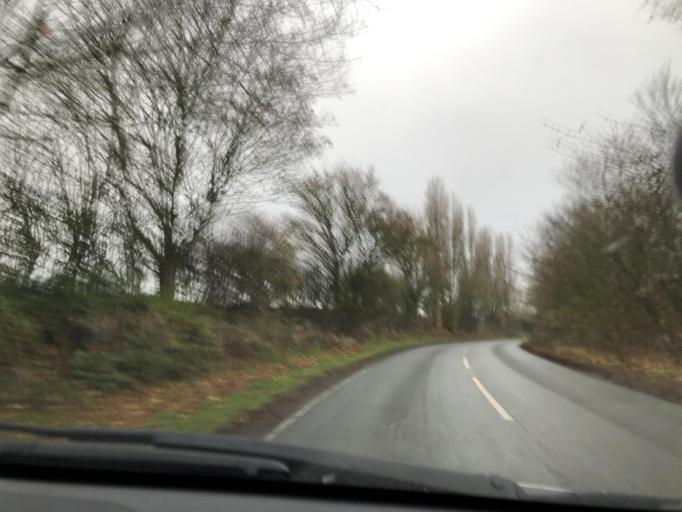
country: GB
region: England
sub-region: Kent
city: Longfield
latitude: 51.4085
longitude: 0.3362
